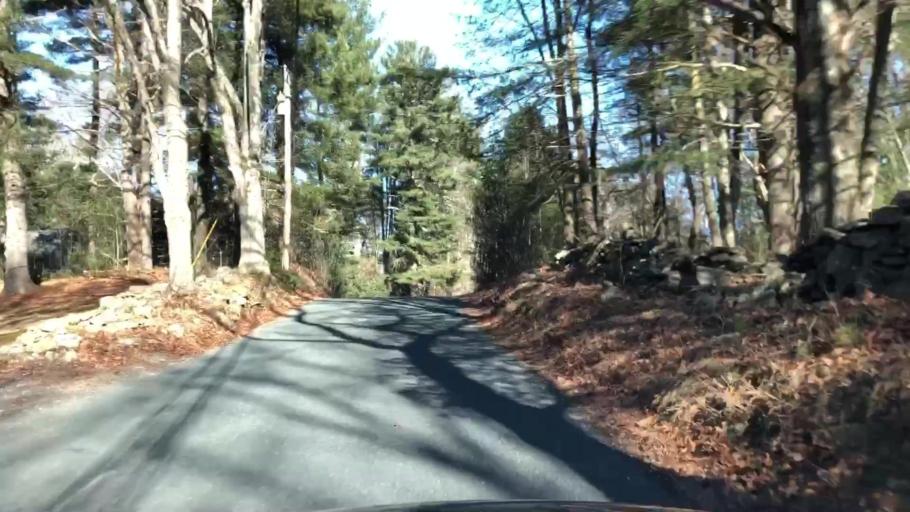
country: US
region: Massachusetts
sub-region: Worcester County
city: Charlton
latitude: 42.1017
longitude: -71.9769
